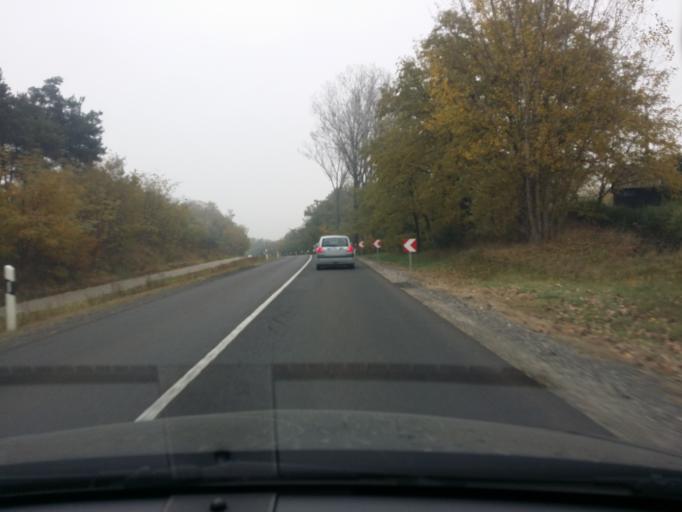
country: HU
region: Szabolcs-Szatmar-Bereg
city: Nyirpazony
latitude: 47.9992
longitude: 21.8159
